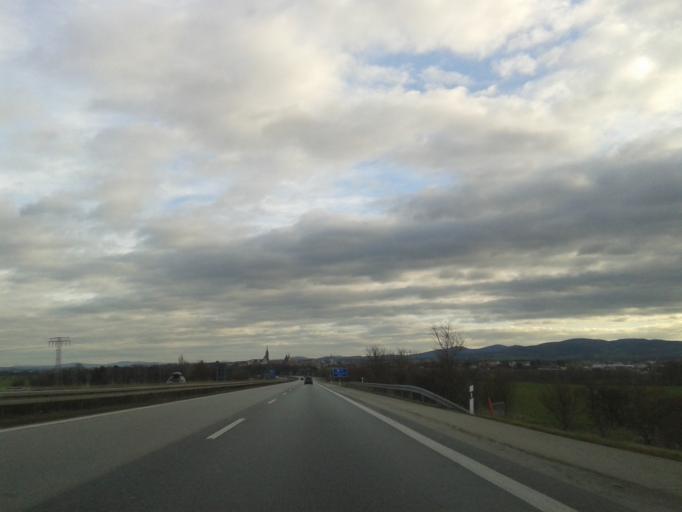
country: DE
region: Saxony
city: Bautzen
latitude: 51.1876
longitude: 14.3871
